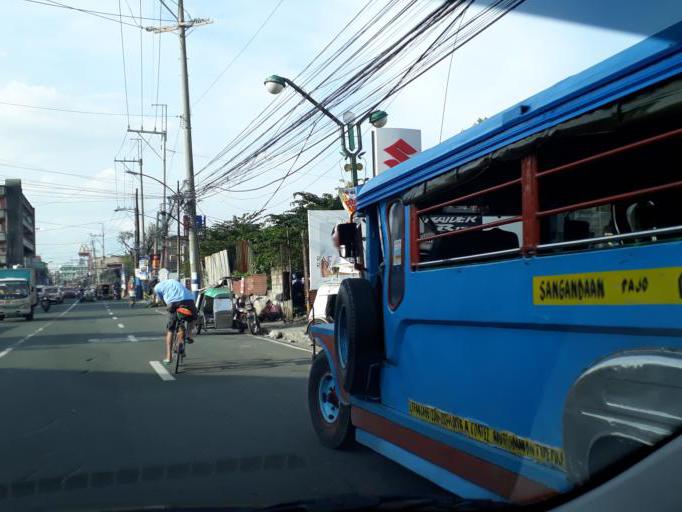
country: PH
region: Metro Manila
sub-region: City of Manila
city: Manila
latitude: 14.6342
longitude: 120.9751
